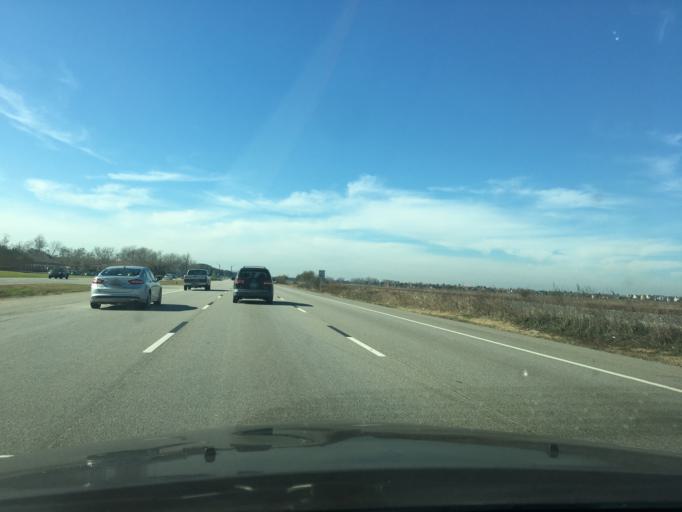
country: US
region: Texas
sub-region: Fort Bend County
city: New Territory
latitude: 29.6082
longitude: -95.6614
